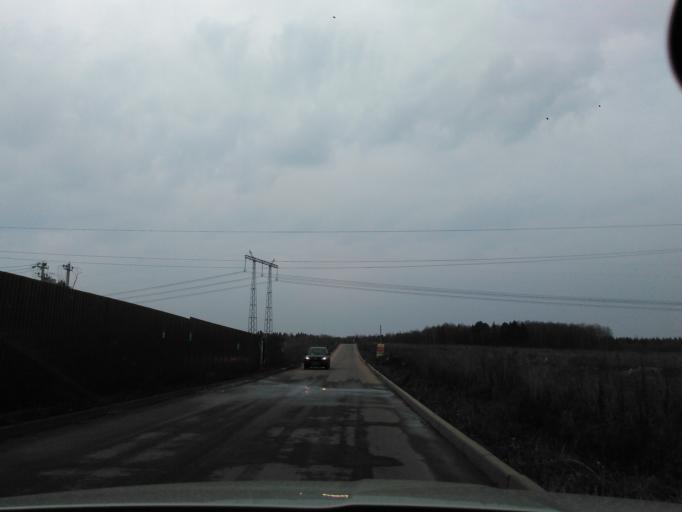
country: RU
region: Moskovskaya
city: Chashnikovo
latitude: 56.0373
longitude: 37.1595
